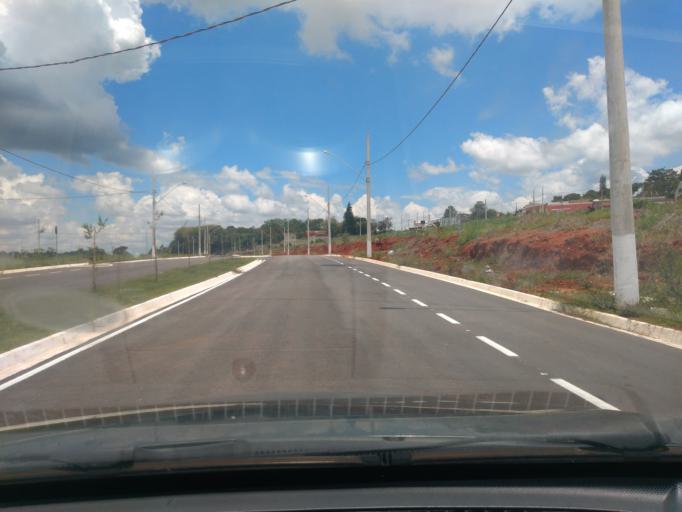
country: BR
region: Minas Gerais
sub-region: Tres Coracoes
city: Tres Coracoes
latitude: -21.6641
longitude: -45.2792
